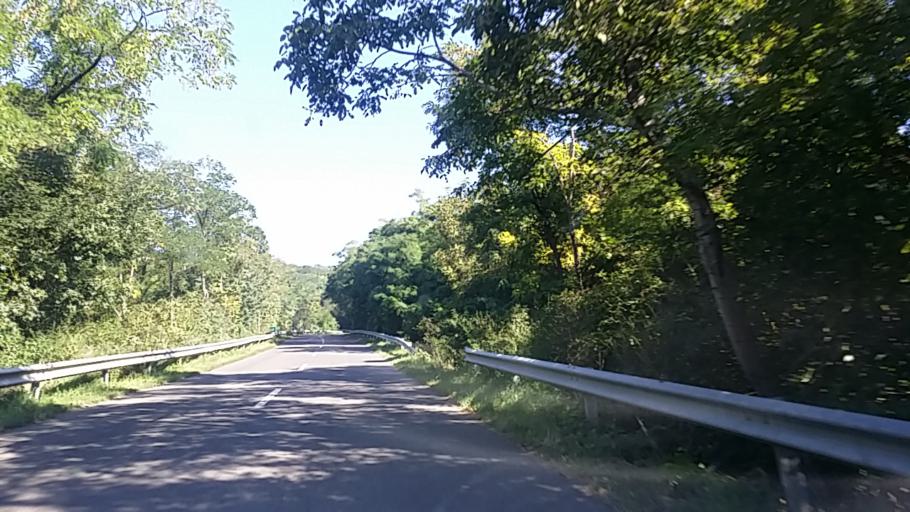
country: HU
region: Nograd
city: Paszto
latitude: 47.9210
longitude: 19.6187
